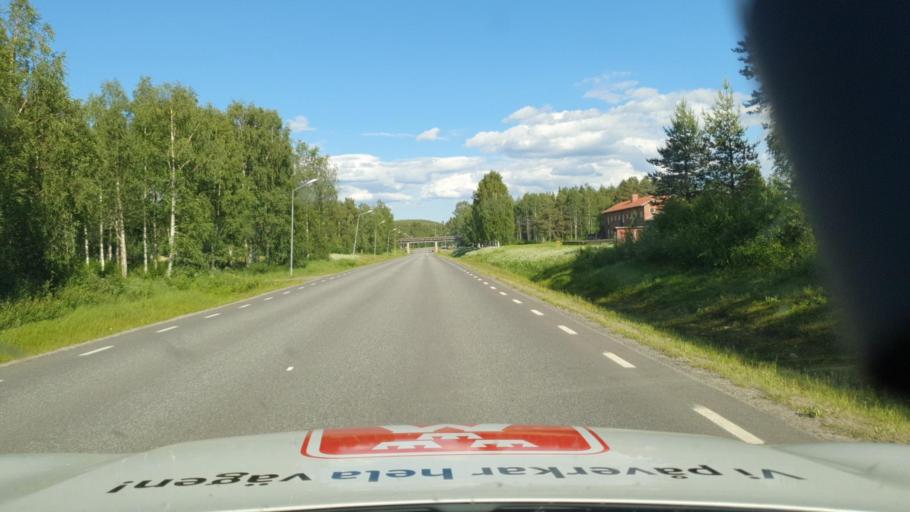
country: SE
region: Vaesterbotten
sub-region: Skelleftea Kommun
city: Langsele
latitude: 64.7933
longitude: 20.0331
